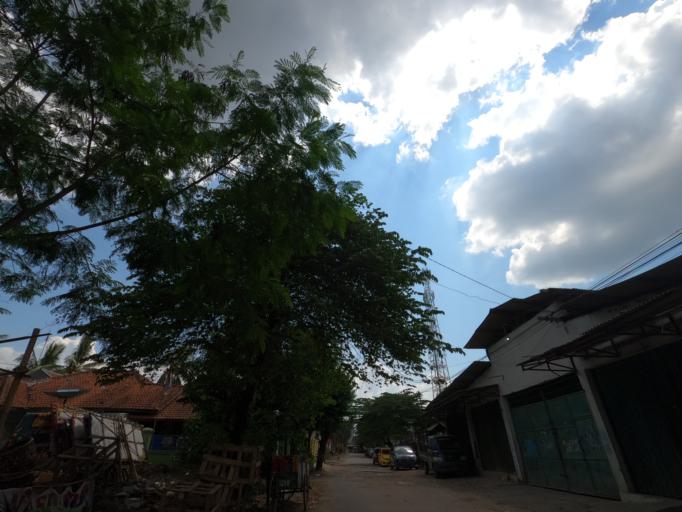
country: ID
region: West Java
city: Pamanukan
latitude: -6.5619
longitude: 107.7668
